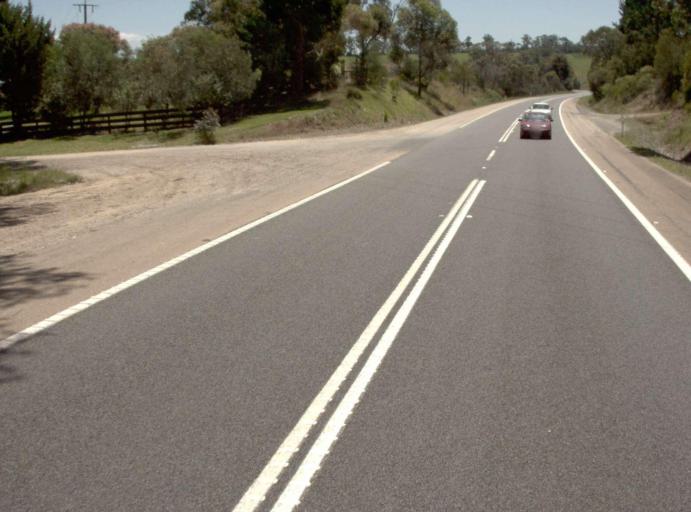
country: AU
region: Victoria
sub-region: East Gippsland
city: Lakes Entrance
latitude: -37.7055
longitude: 148.5679
